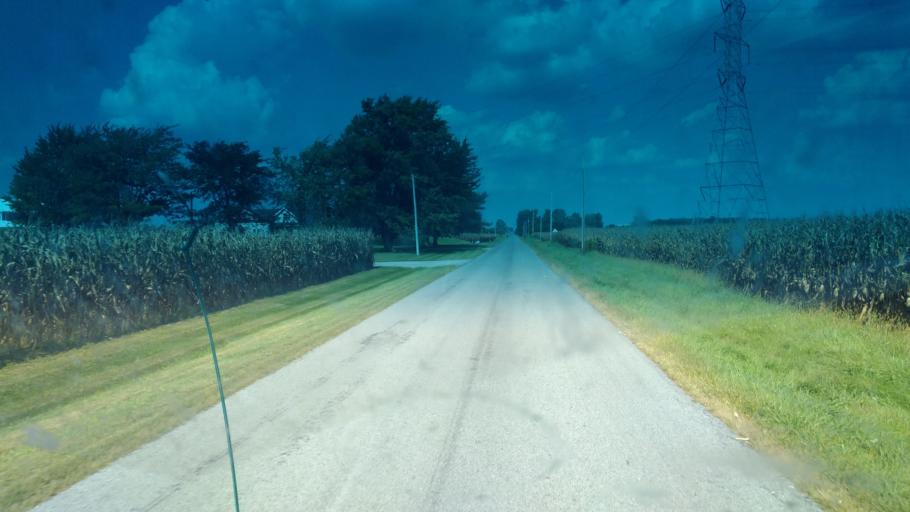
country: US
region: Ohio
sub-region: Hardin County
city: Ada
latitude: 40.6899
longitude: -83.8800
